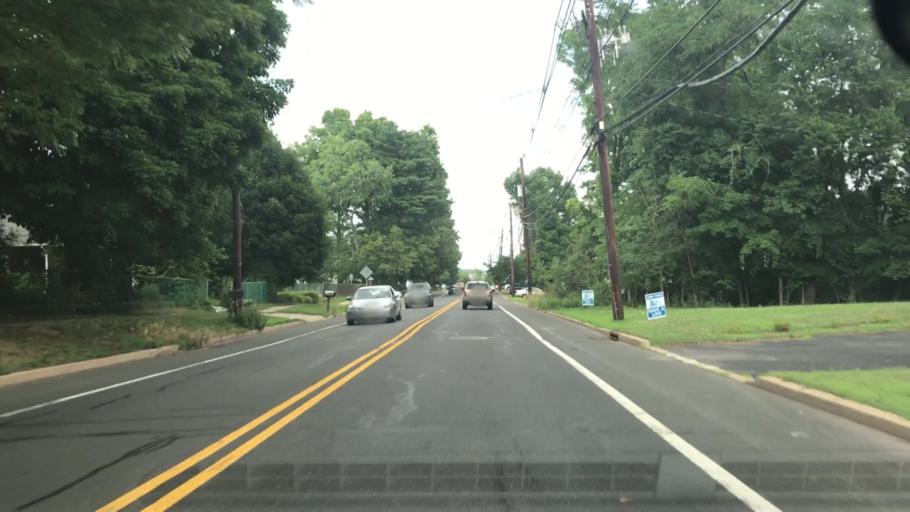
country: US
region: New Jersey
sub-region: Somerset County
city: Bradley Gardens
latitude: 40.5574
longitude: -74.6584
